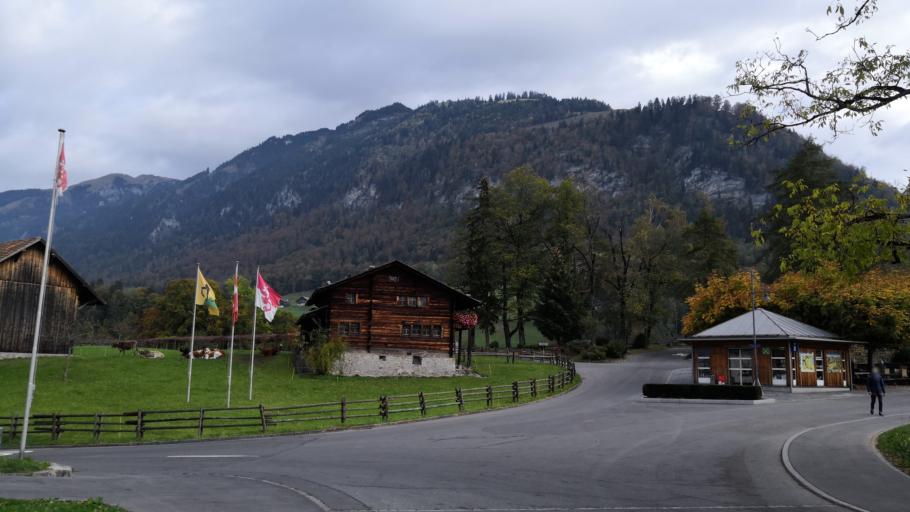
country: CH
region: Obwalden
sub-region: Obwalden
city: Kerns
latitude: 46.8720
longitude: 8.2687
